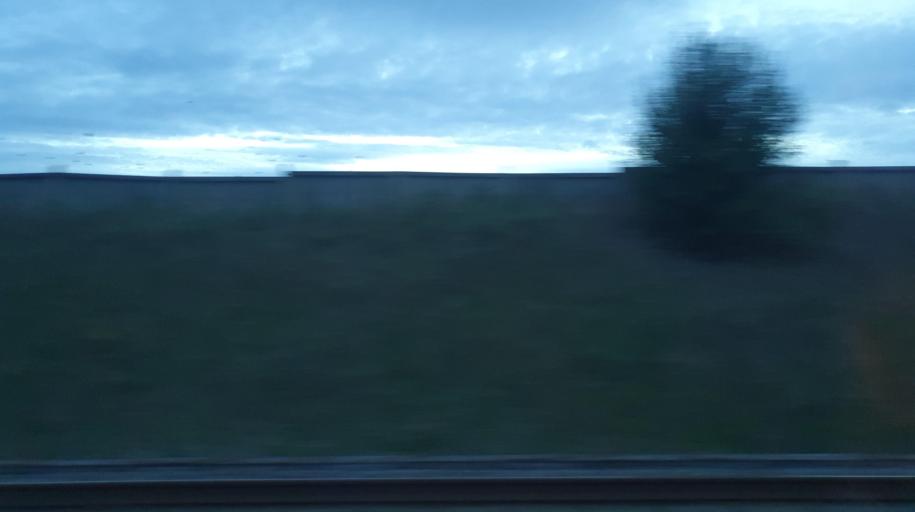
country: NO
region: Vestfold
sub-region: Sande
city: Sande
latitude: 59.5829
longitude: 10.2061
